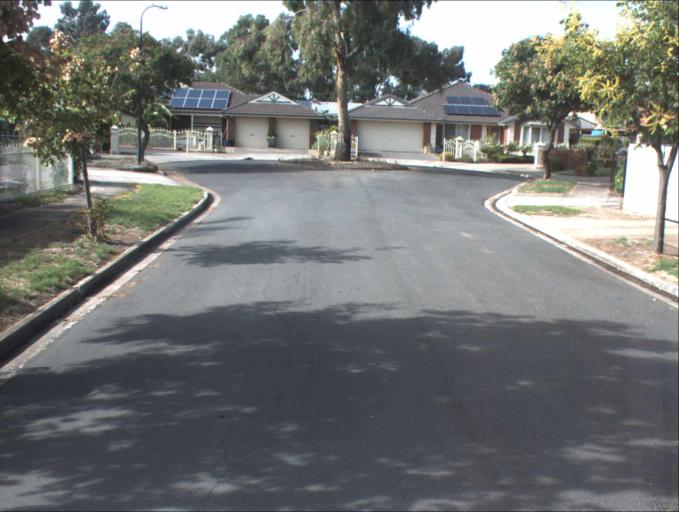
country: AU
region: South Australia
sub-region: Charles Sturt
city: Woodville North
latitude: -34.8638
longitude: 138.5613
